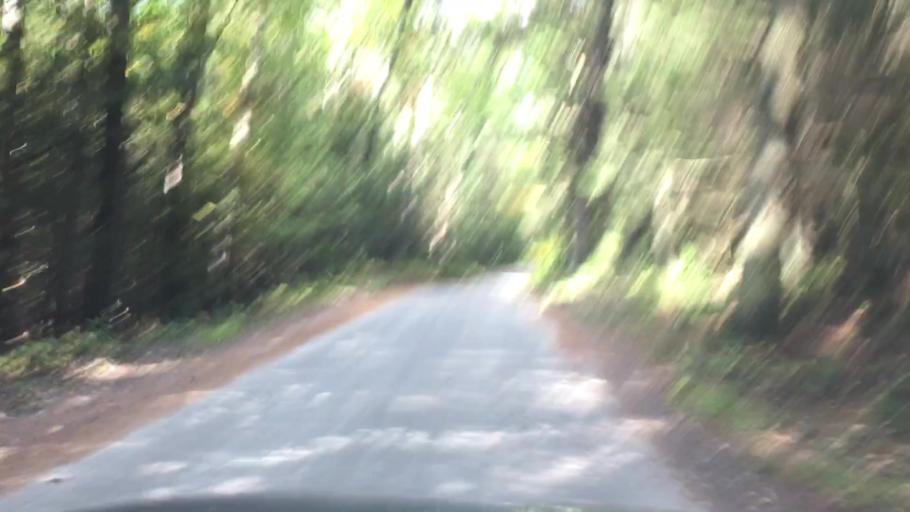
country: US
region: Connecticut
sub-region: Tolland County
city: Stafford
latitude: 41.9860
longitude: -72.3300
